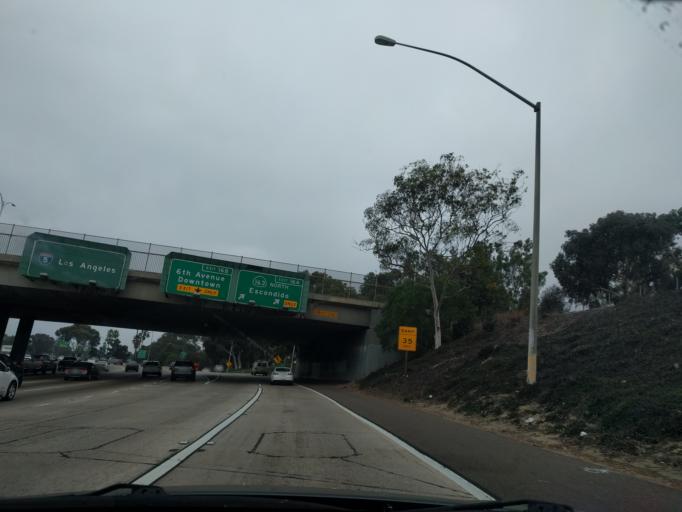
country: US
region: California
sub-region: San Diego County
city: San Diego
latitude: 32.7240
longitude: -117.1506
